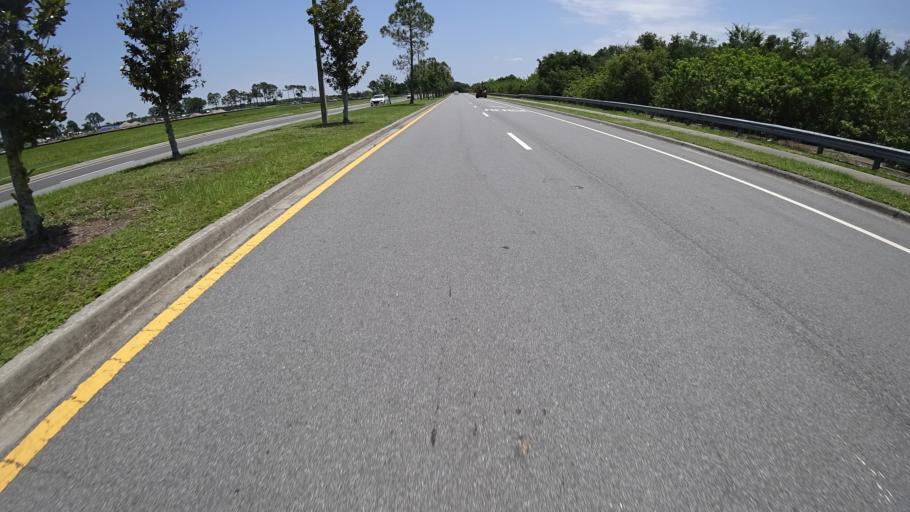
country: US
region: Florida
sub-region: Sarasota County
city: Desoto Lakes
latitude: 27.4254
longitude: -82.4919
